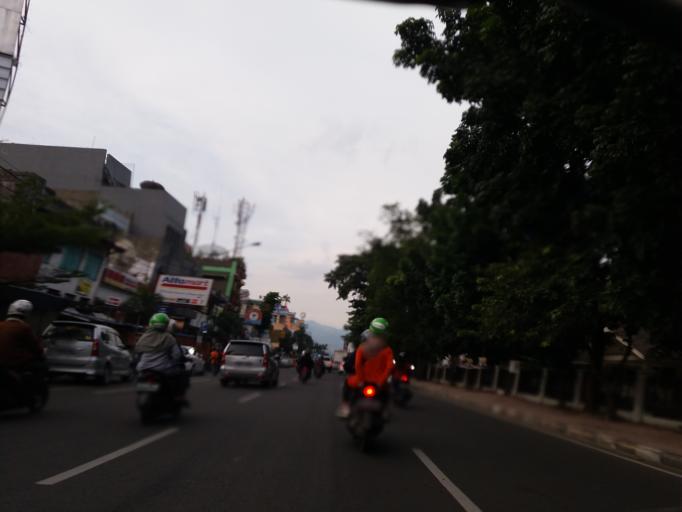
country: ID
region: West Java
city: Bandung
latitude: -6.9112
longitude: 107.6387
